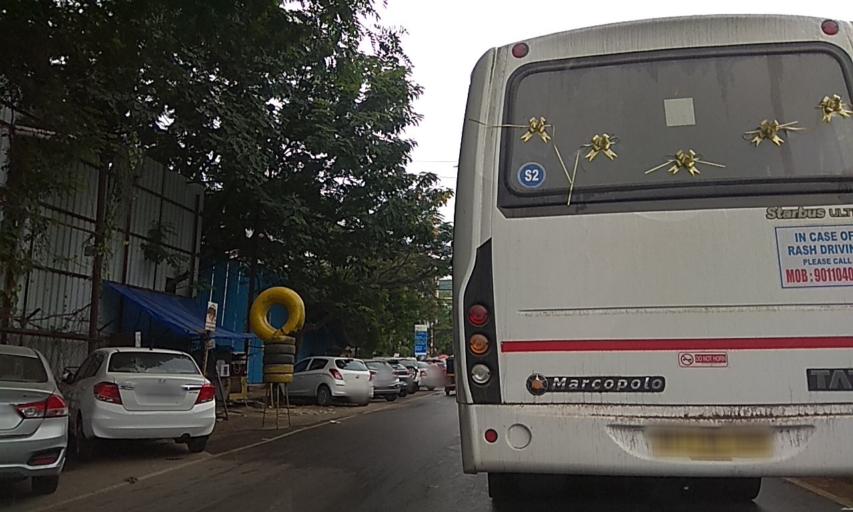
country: IN
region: Maharashtra
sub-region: Pune Division
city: Lohogaon
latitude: 18.5643
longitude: 73.9181
